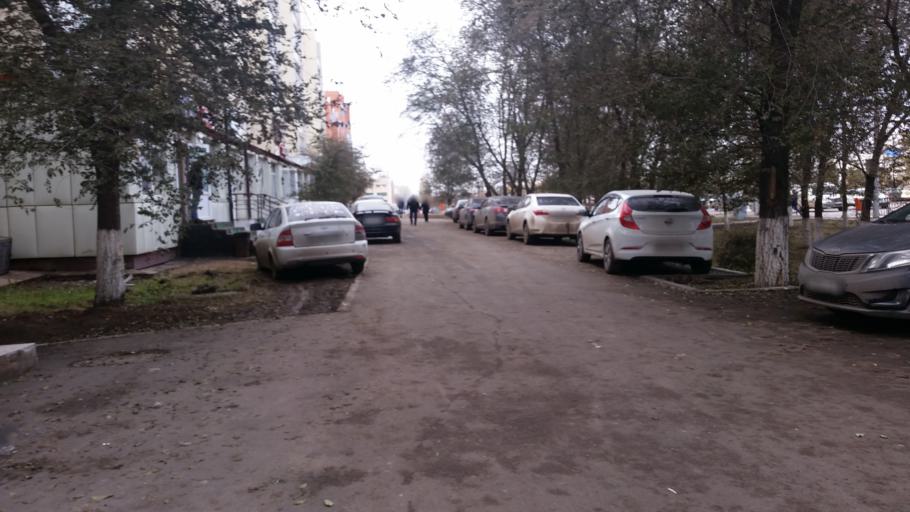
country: KZ
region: Astana Qalasy
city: Astana
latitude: 51.1550
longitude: 71.4708
